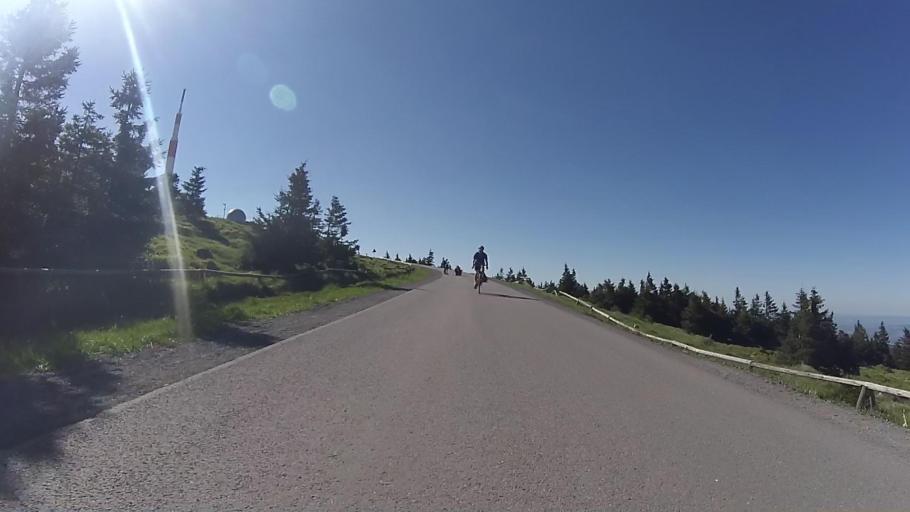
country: DE
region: Lower Saxony
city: Braunlage
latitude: 51.7997
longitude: 10.6195
